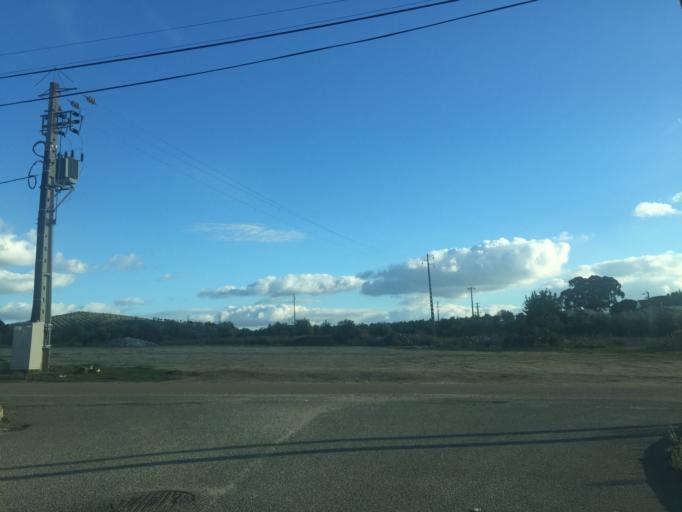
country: PT
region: Portalegre
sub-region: Alter do Chao
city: Alter do Chao
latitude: 39.1943
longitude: -7.6546
